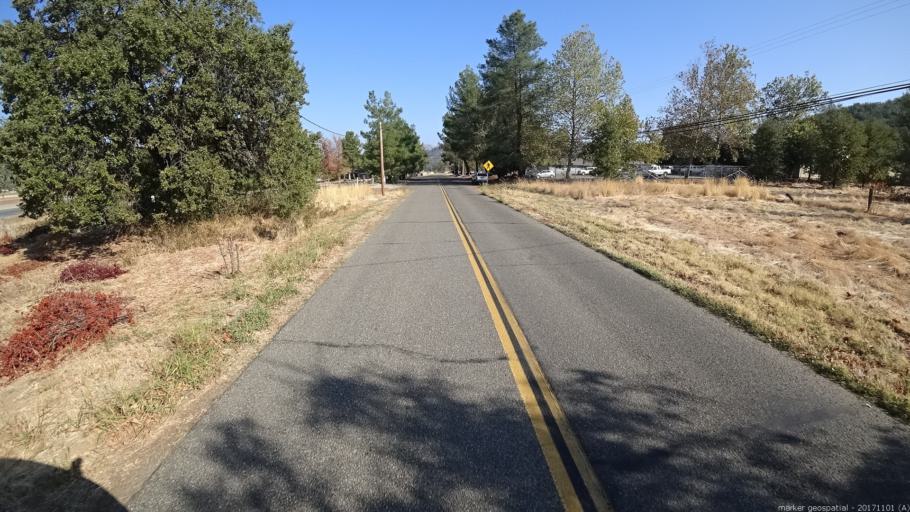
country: US
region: California
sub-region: Shasta County
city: Shasta Lake
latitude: 40.7012
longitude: -122.3391
